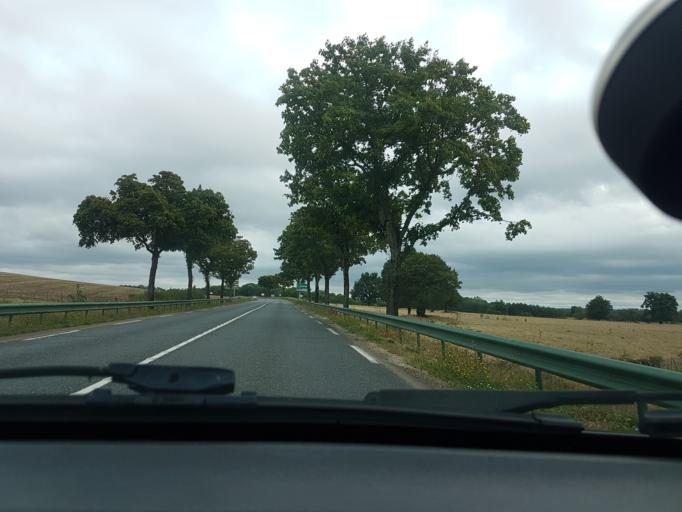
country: FR
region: Bourgogne
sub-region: Departement de l'Yonne
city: Avallon
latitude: 47.5055
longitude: 3.8638
